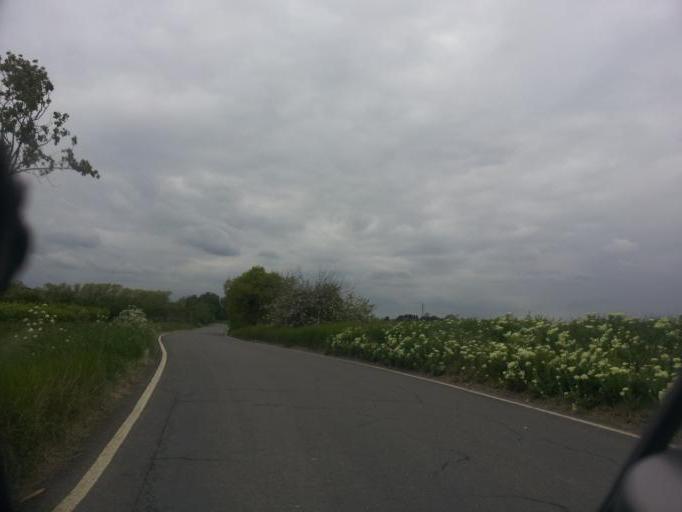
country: GB
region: England
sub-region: Kent
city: Newington
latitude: 51.3818
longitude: 0.7036
